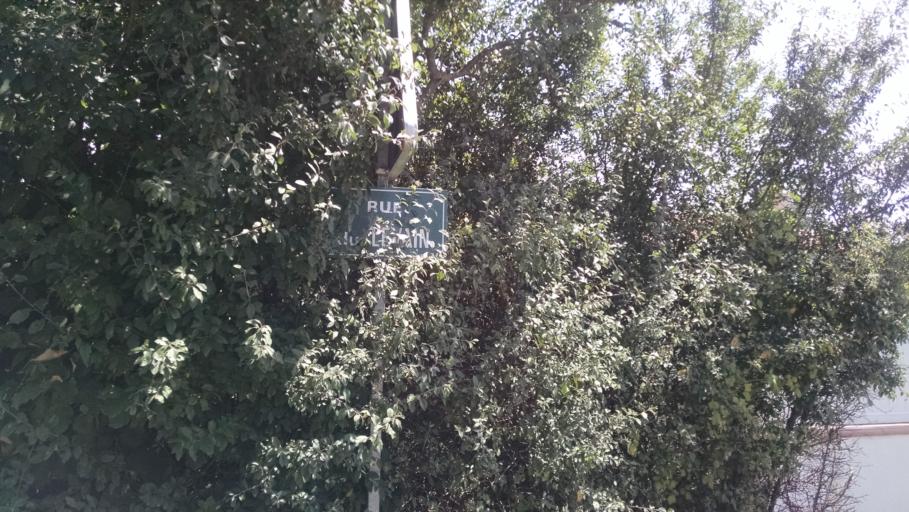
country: FR
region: Pays de la Loire
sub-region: Departement de la Loire-Atlantique
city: Clisson
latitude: 47.1074
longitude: -1.2729
